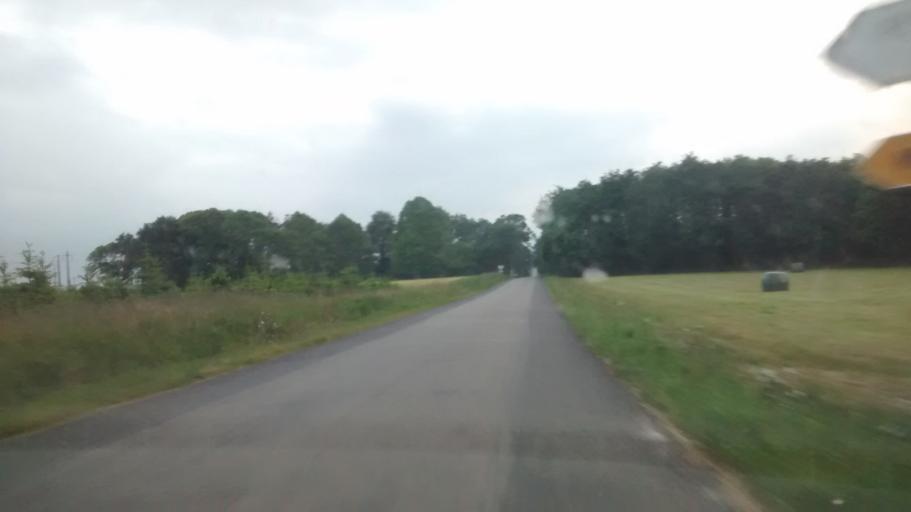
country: FR
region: Brittany
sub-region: Departement du Morbihan
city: Saint-Martin-sur-Oust
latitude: 47.7299
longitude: -2.2913
